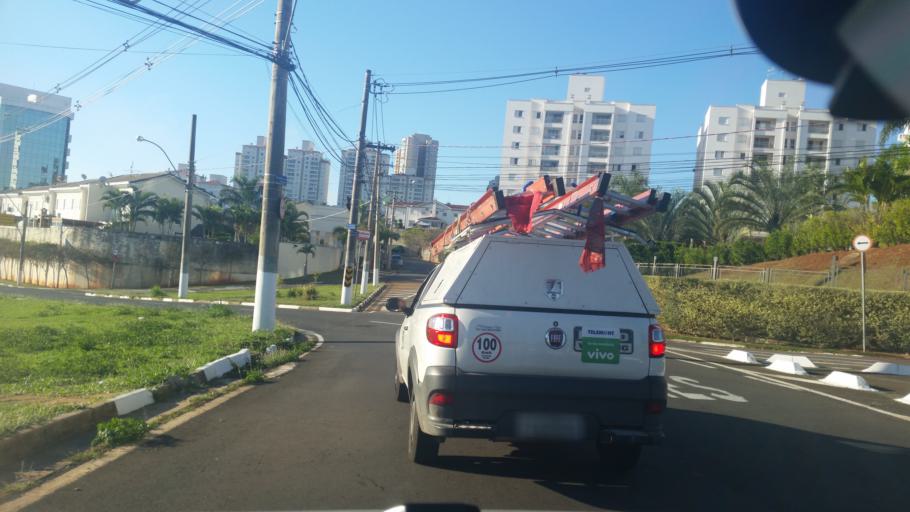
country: BR
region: Sao Paulo
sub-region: Campinas
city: Campinas
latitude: -22.8587
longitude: -47.0543
